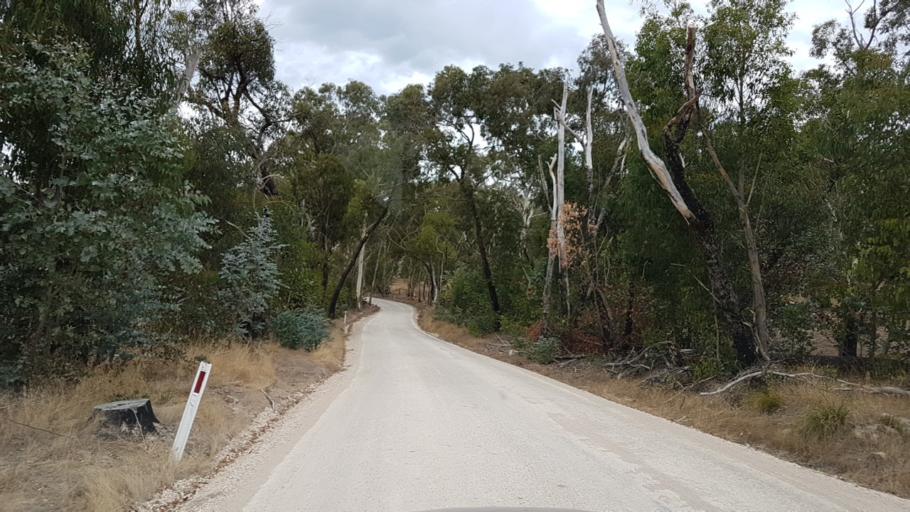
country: AU
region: South Australia
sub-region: Adelaide Hills
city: Gumeracha
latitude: -34.7826
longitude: 138.8380
